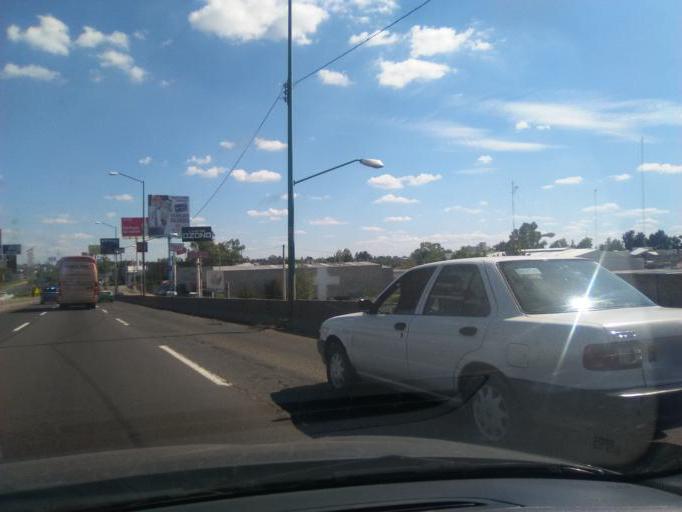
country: MX
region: Guanajuato
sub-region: Leon
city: Fraccionamiento Paraiso Real
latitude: 21.0895
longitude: -101.6199
